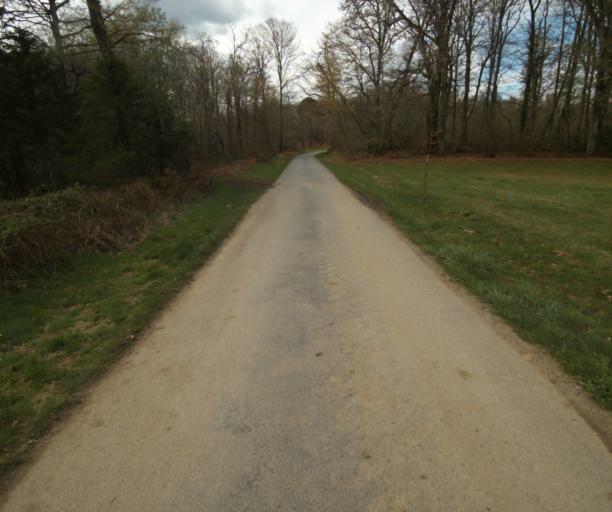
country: FR
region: Limousin
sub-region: Departement de la Correze
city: Argentat
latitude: 45.1920
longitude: 1.9250
